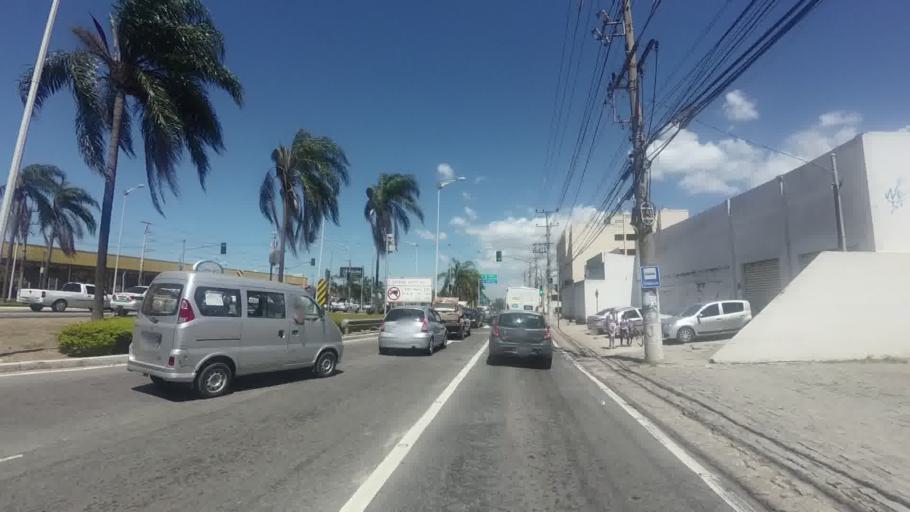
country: BR
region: Espirito Santo
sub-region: Vila Velha
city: Vila Velha
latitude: -20.2355
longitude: -40.2768
